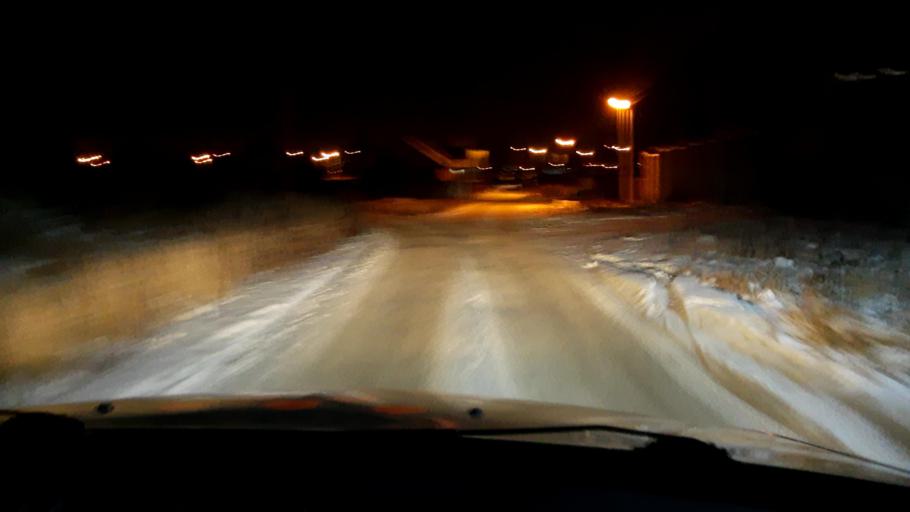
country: RU
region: Bashkortostan
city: Mikhaylovka
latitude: 54.8005
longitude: 55.8808
